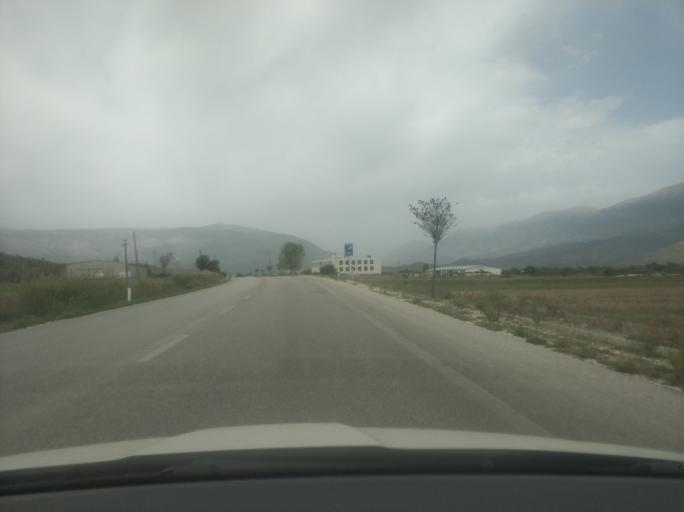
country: AL
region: Gjirokaster
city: Gjirokaster
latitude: 40.1163
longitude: 20.1181
